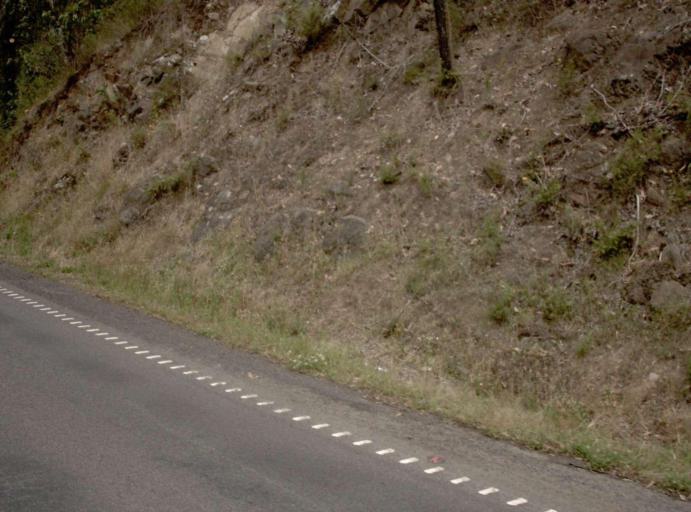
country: AU
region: Victoria
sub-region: Yarra Ranges
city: Yarra Glen
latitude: -37.5383
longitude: 145.4151
